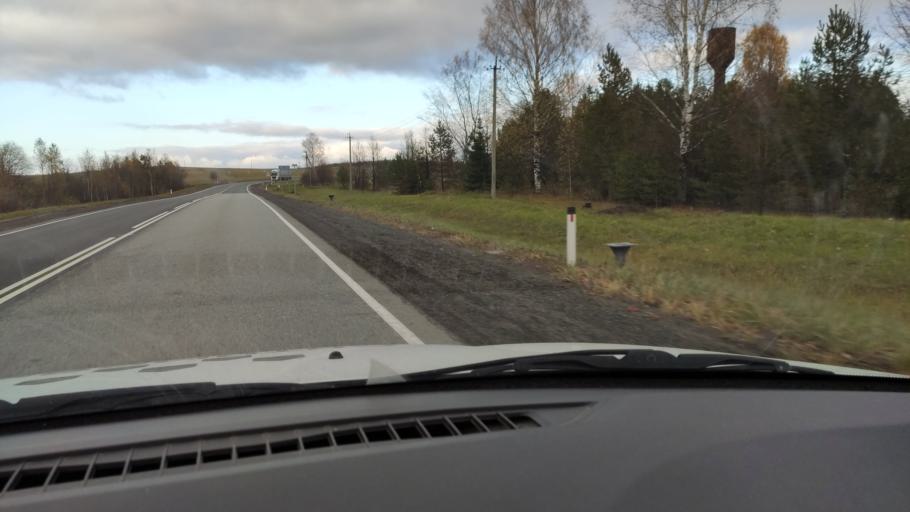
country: RU
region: Kirov
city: Belaya Kholunitsa
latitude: 58.8889
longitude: 50.8752
